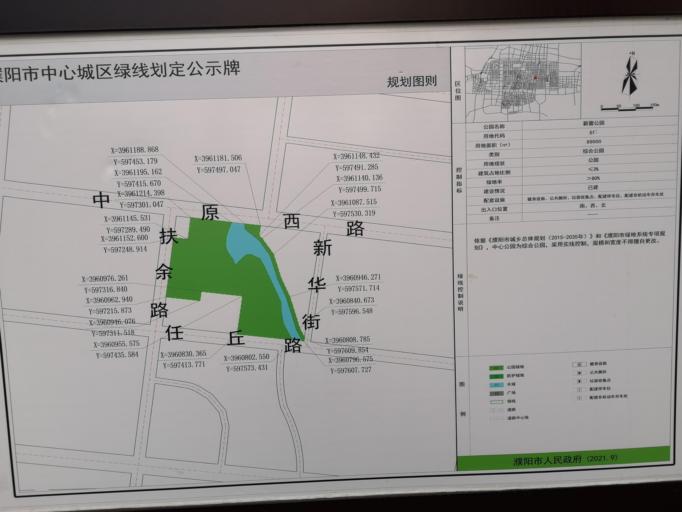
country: CN
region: Henan Sheng
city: Zhongyuanlu
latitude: 35.7750
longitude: 115.0770
